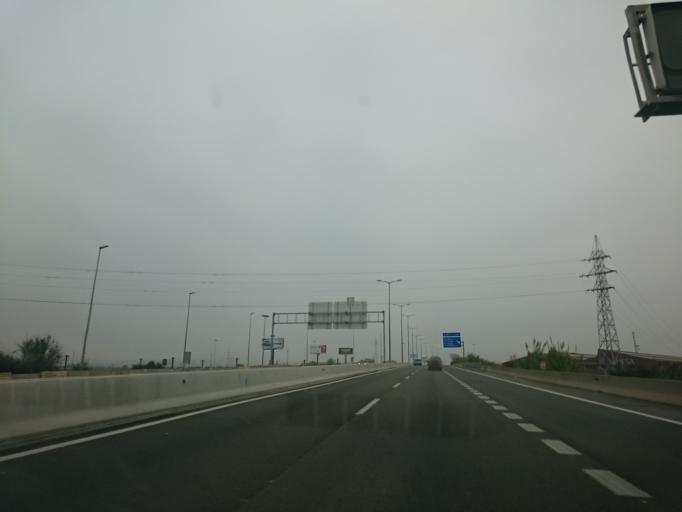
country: ES
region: Catalonia
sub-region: Provincia de Barcelona
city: El Prat de Llobregat
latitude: 41.3253
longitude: 2.0777
